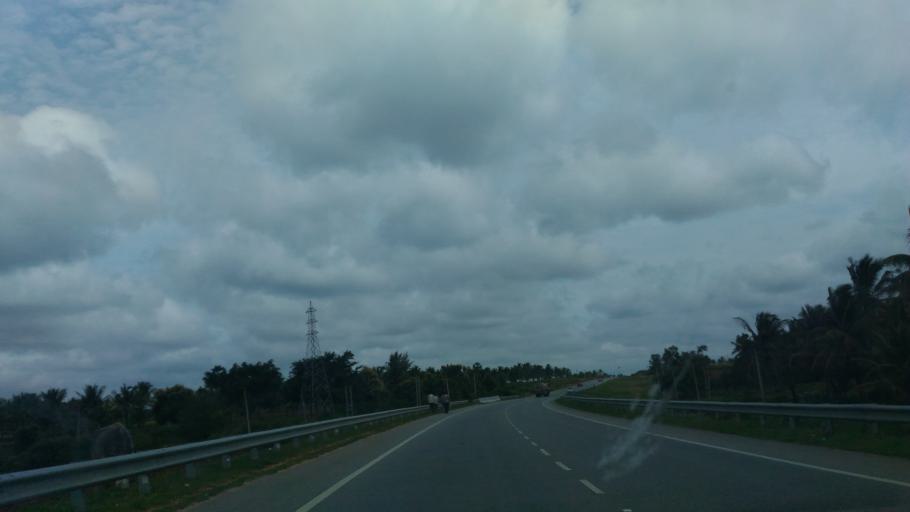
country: IN
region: Karnataka
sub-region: Hassan
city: Channarayapatna
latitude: 12.9089
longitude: 76.4212
